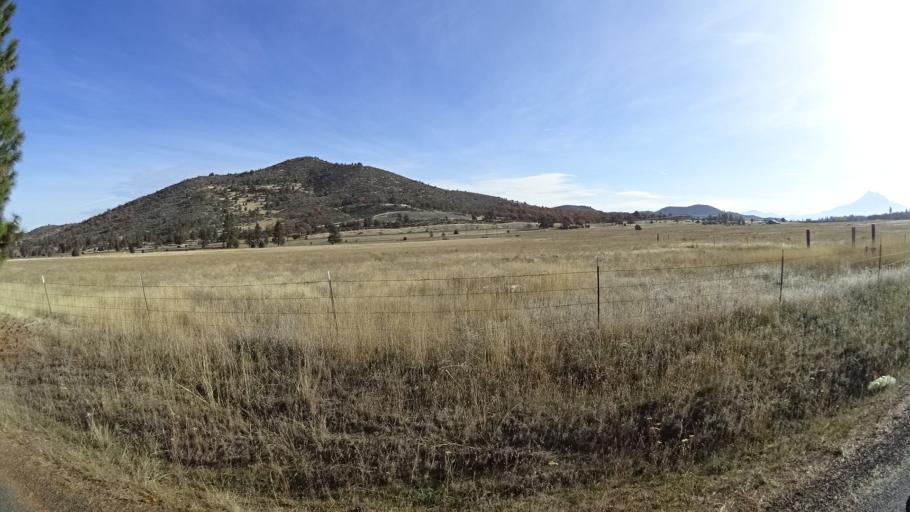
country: US
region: California
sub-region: Siskiyou County
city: Yreka
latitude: 41.6763
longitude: -122.6329
